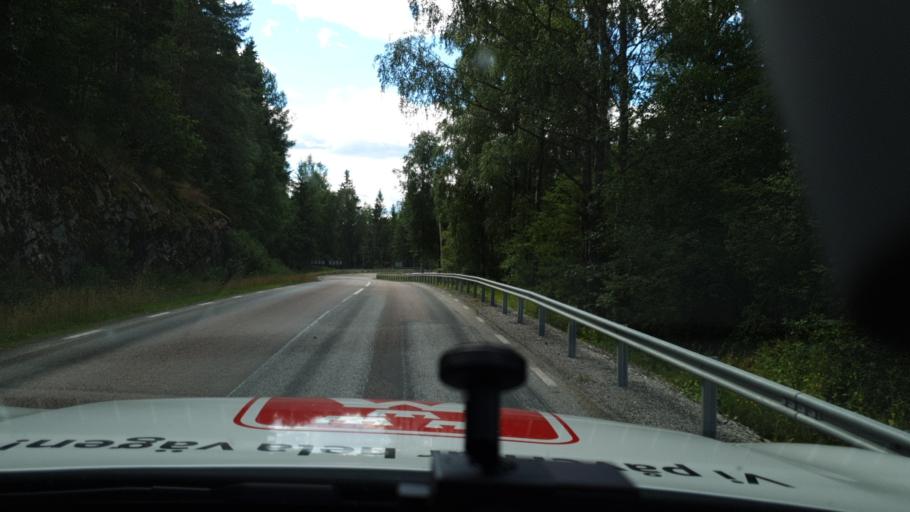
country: SE
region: Vaermland
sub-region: Sunne Kommun
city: Sunne
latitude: 59.6558
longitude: 12.9457
